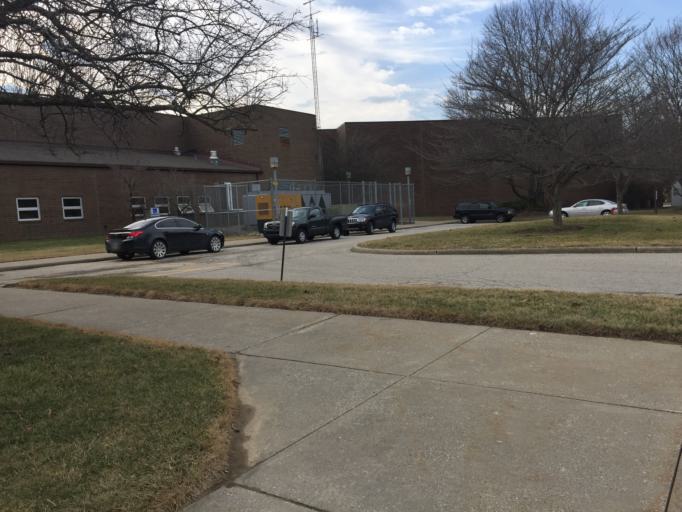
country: US
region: Kentucky
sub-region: Jefferson County
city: Valley Station
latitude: 38.1136
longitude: -85.8447
